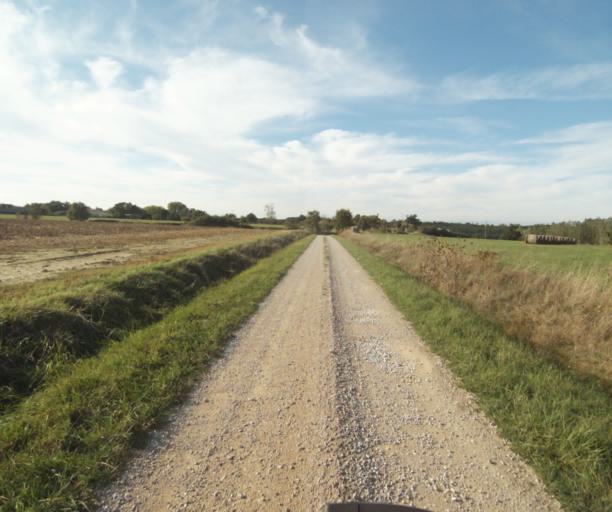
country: FR
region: Midi-Pyrenees
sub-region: Departement du Tarn-et-Garonne
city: Finhan
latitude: 43.9175
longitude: 1.1162
